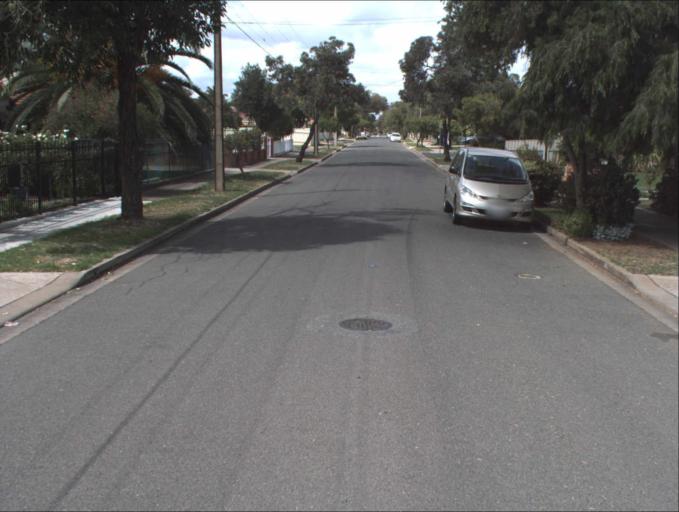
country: AU
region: South Australia
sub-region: Port Adelaide Enfield
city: Blair Athol
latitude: -34.8536
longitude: 138.5946
